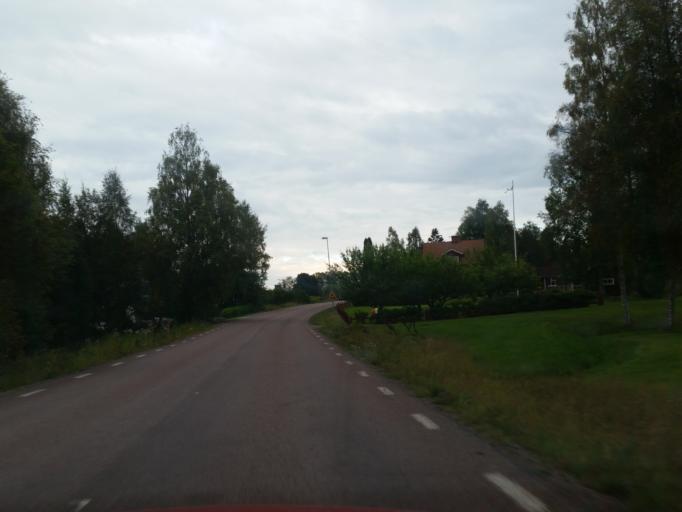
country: SE
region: Dalarna
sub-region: Leksand Municipality
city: Smedby
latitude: 60.6771
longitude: 15.1278
